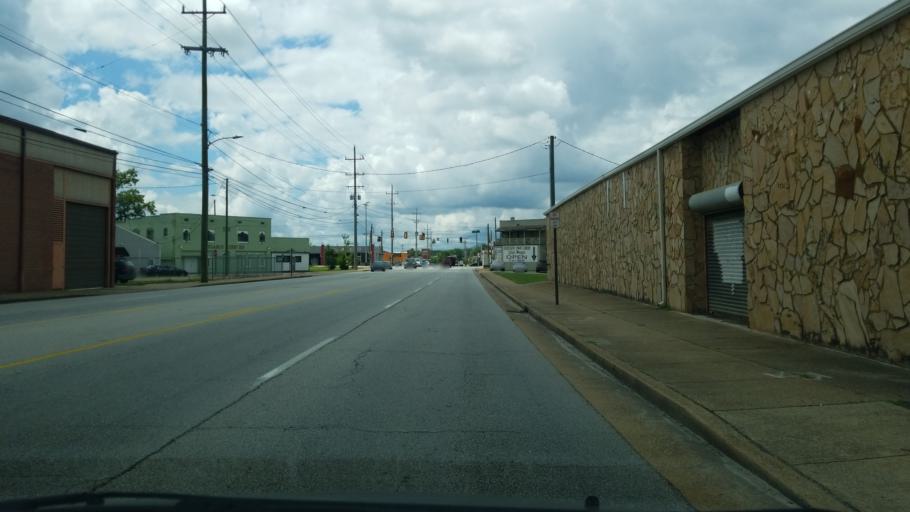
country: US
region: Tennessee
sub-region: Hamilton County
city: Chattanooga
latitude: 35.0332
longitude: -85.2957
